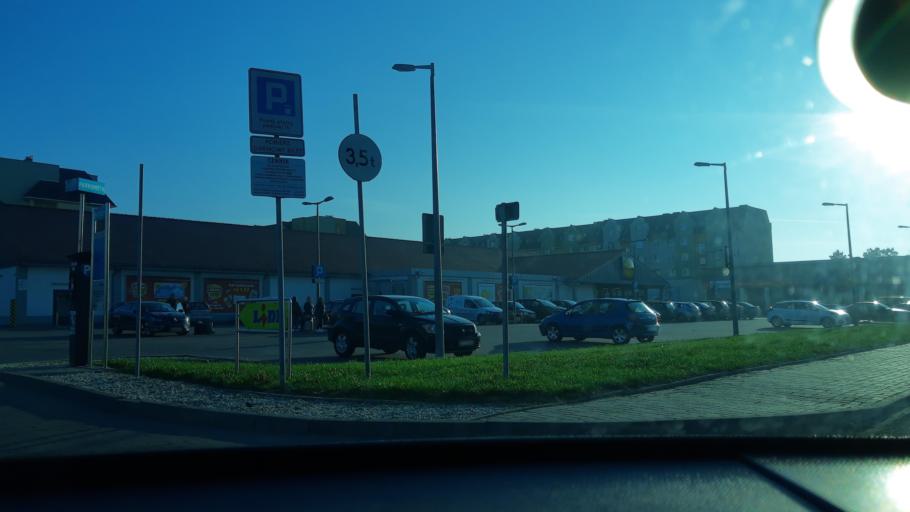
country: PL
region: Lodz Voivodeship
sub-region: Powiat sieradzki
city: Sieradz
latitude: 51.5932
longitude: 18.7256
